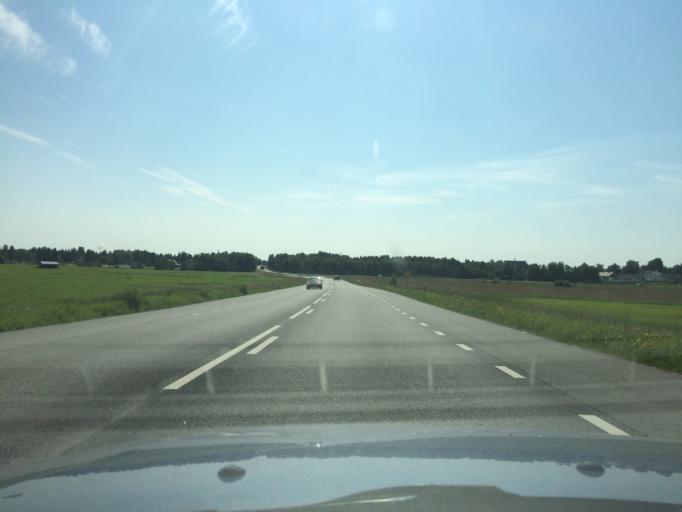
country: SE
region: Norrbotten
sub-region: Pitea Kommun
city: Bergsviken
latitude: 65.3550
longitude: 21.4015
